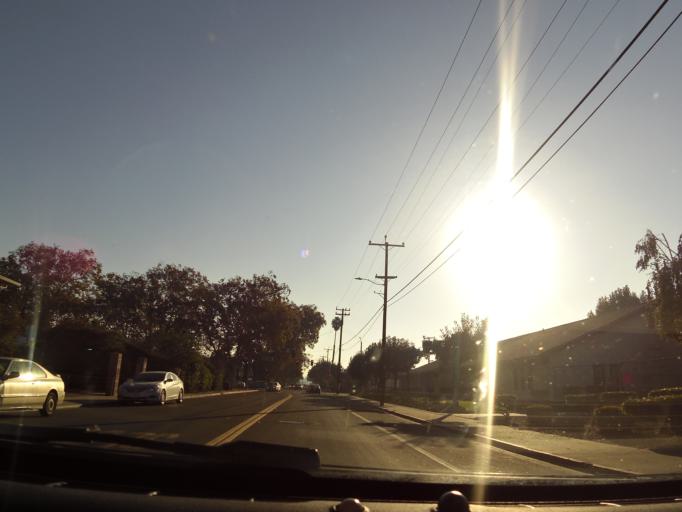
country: US
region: California
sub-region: San Benito County
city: Hollister
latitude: 36.8398
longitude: -121.4036
